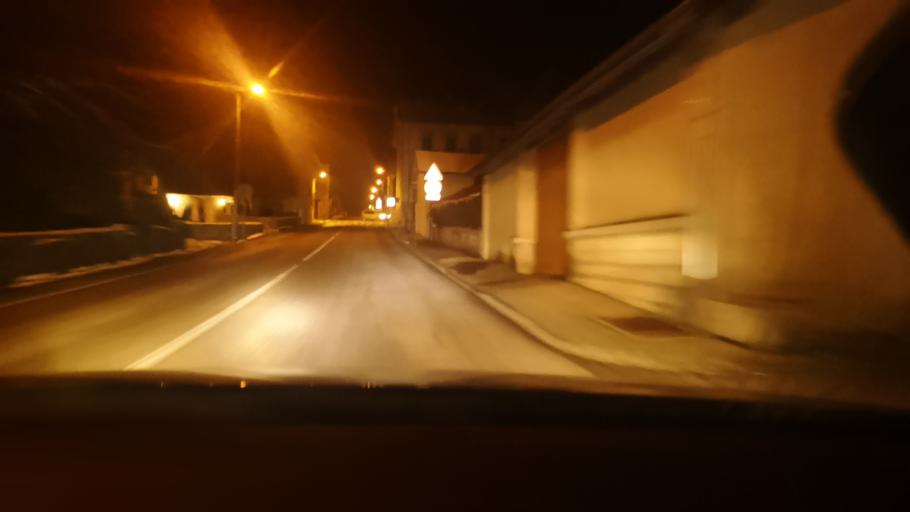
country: FR
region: Rhone-Alpes
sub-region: Departement de l'Ain
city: Villereversure
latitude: 46.1592
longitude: 5.4184
